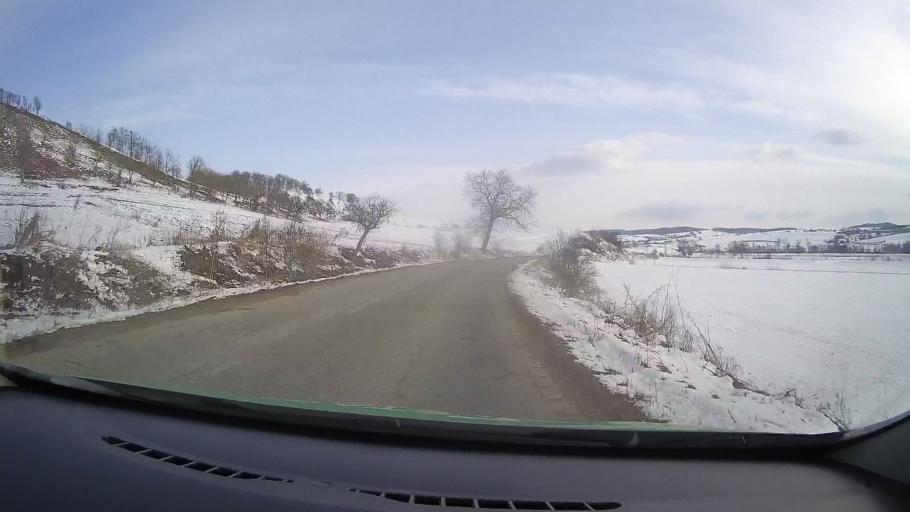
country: RO
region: Sibiu
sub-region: Comuna Merghindeal
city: Merghindeal
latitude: 45.9778
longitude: 24.7046
